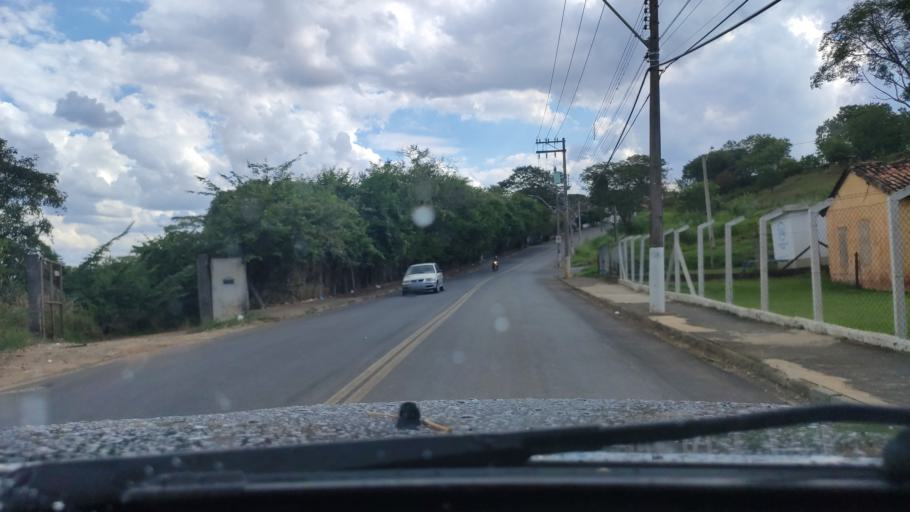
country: BR
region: Sao Paulo
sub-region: Itapira
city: Itapira
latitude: -22.4372
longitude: -46.8059
